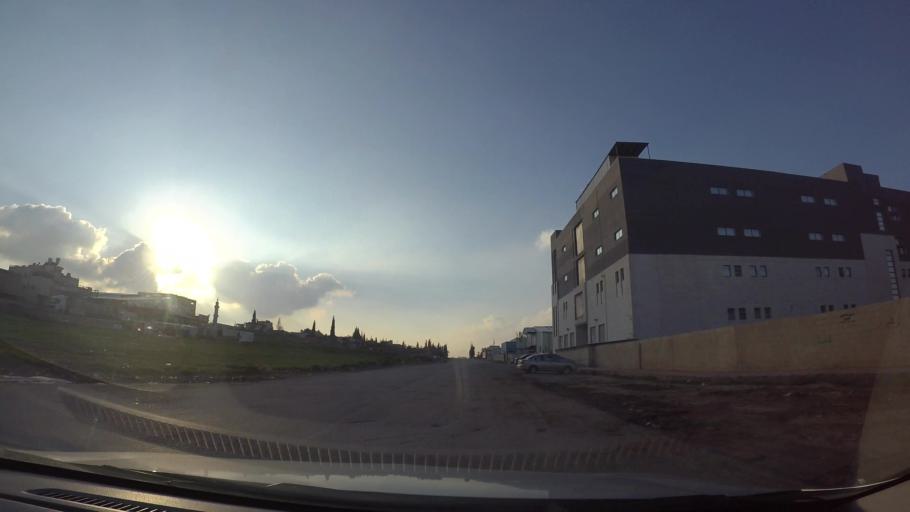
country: JO
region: Amman
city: Al Bunayyat ash Shamaliyah
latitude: 31.9096
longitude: 35.9186
